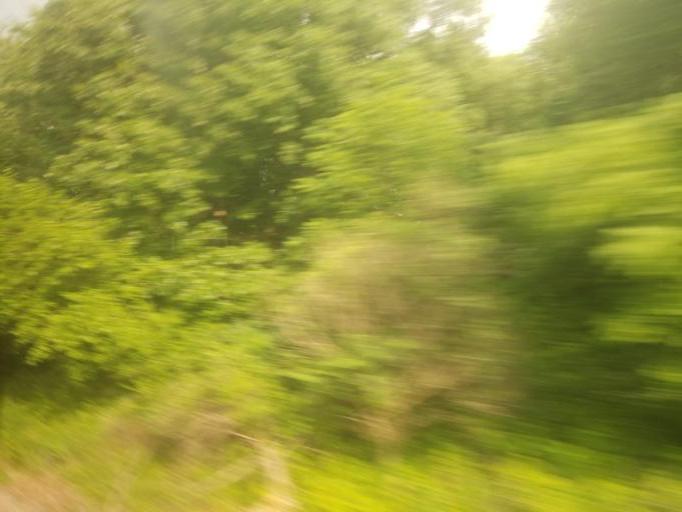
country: US
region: Illinois
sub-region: Bureau County
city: Princeton
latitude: 41.3712
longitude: -89.5639
